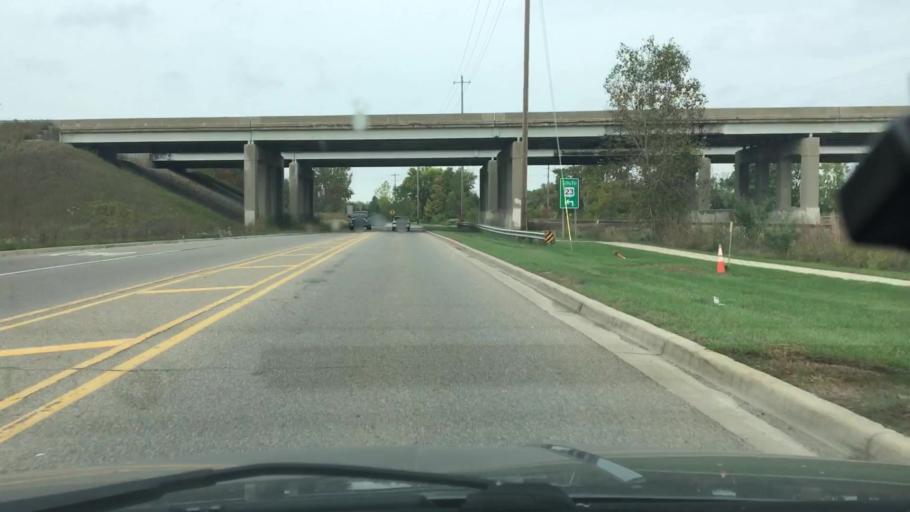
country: US
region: Michigan
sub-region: Genesee County
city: Fenton
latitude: 42.8038
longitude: -83.7269
